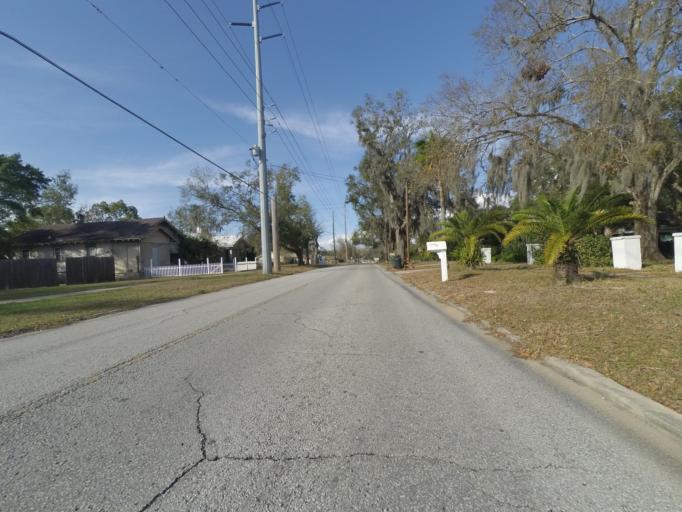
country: US
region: Florida
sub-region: Lake County
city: Eustis
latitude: 28.8404
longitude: -81.6835
